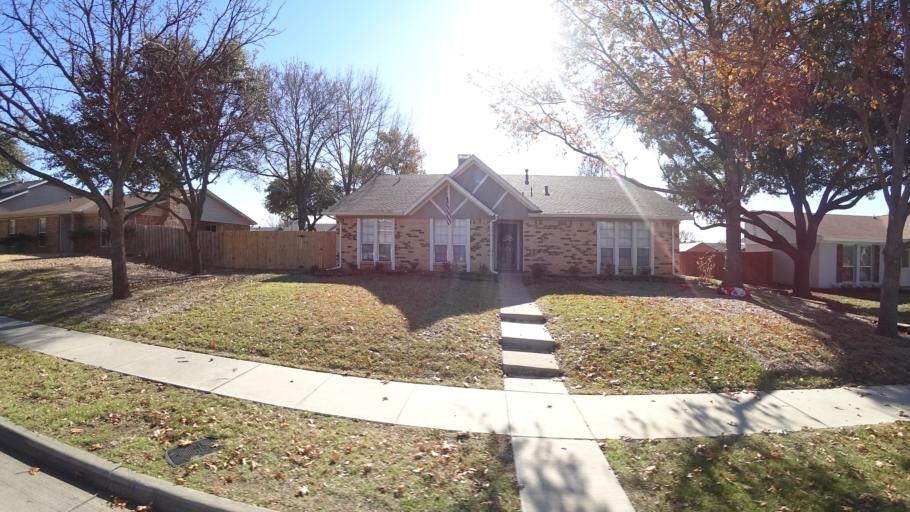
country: US
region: Texas
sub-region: Denton County
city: Lewisville
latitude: 33.0306
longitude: -97.0206
